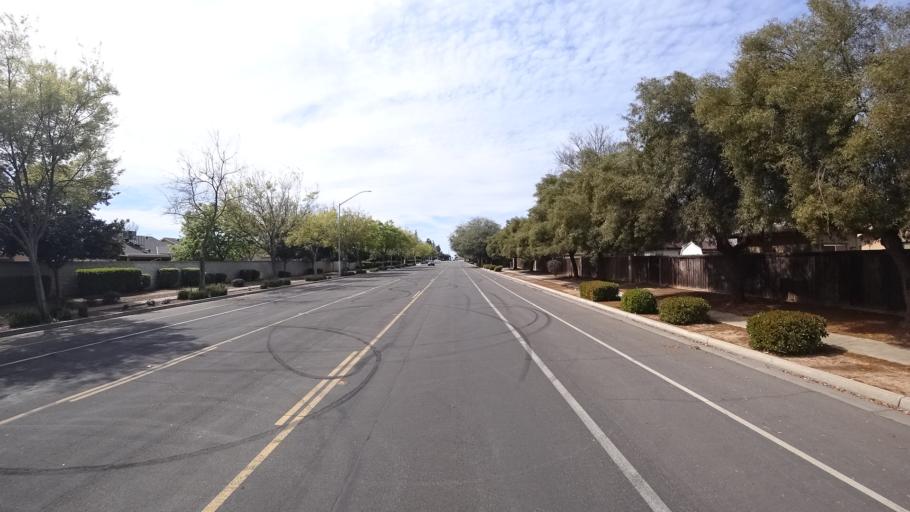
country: US
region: California
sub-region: Fresno County
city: West Park
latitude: 36.8009
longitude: -119.8863
